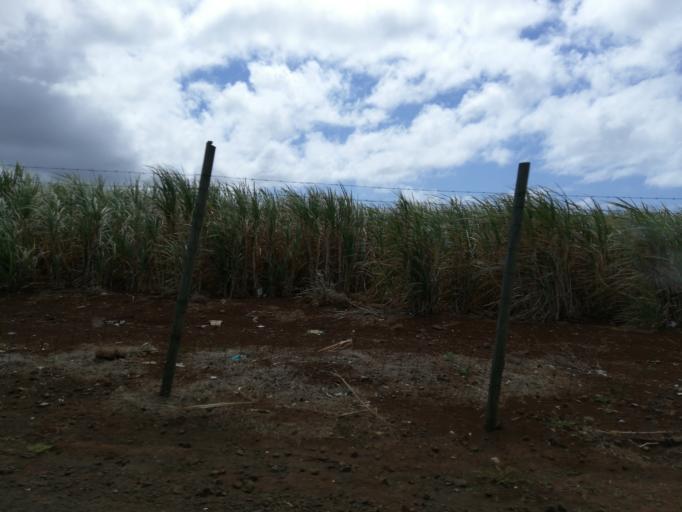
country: MU
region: Riviere du Rempart
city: Esperance Trebuchet
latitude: -20.0652
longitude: 57.6741
